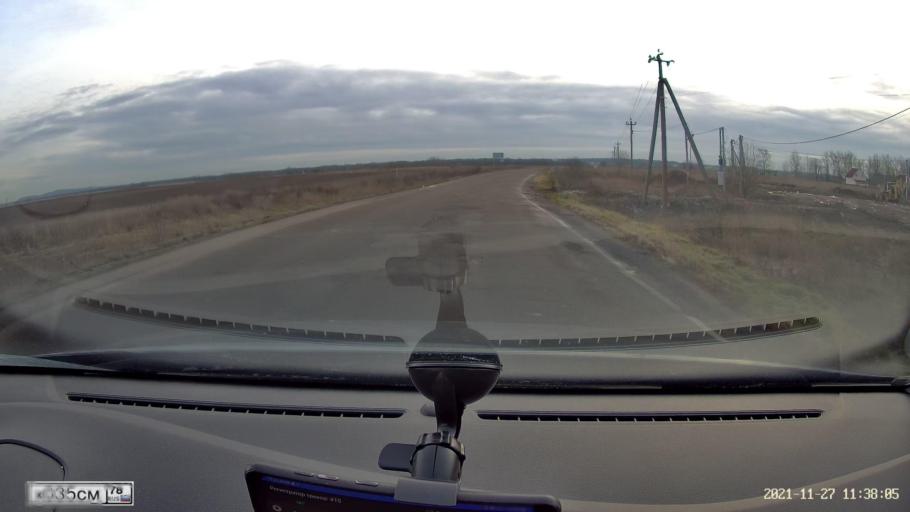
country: RU
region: Leningrad
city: Russko-Vysotskoye
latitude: 59.6910
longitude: 29.9956
